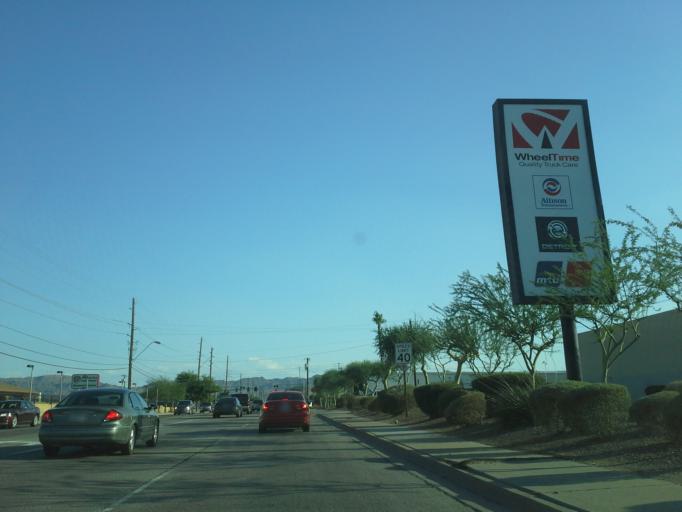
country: US
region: Arizona
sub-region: Maricopa County
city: Phoenix
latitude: 33.4244
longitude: -112.0999
